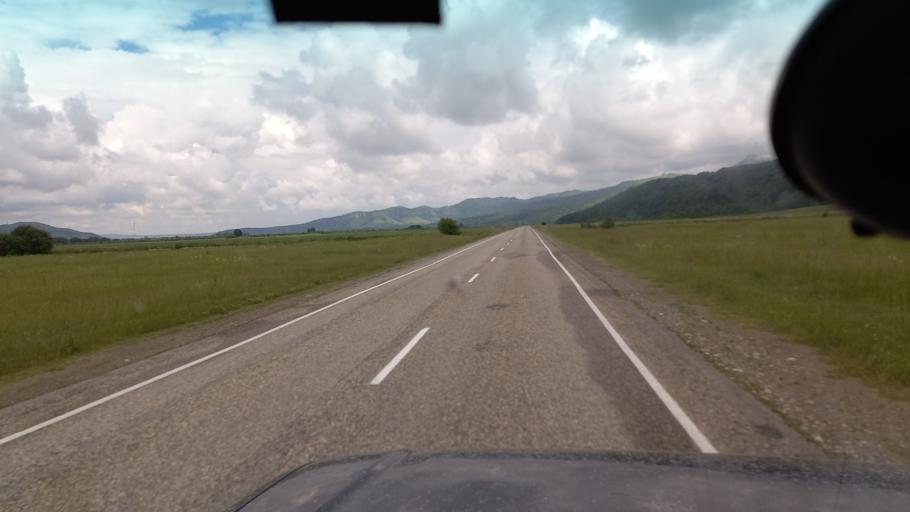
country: RU
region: Krasnodarskiy
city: Psebay
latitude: 44.0923
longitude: 40.8041
